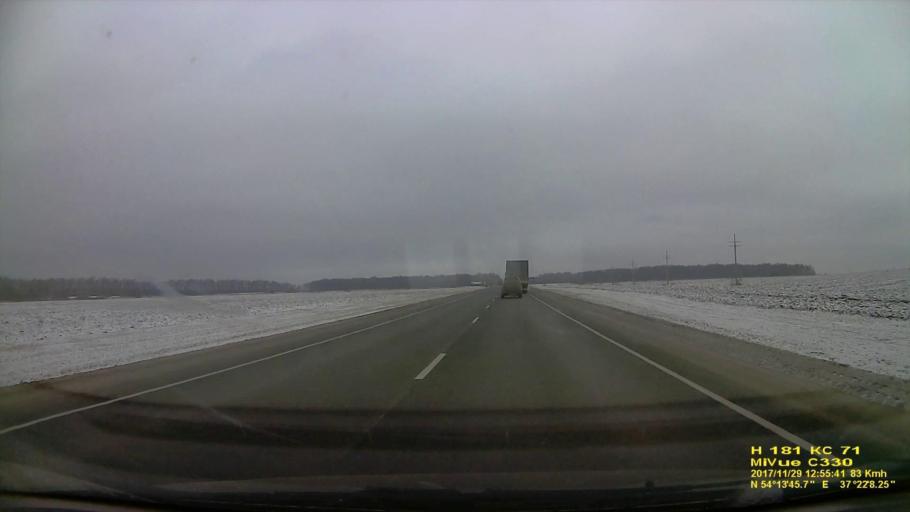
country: RU
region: Tula
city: Leninskiy
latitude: 54.2294
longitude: 37.3688
